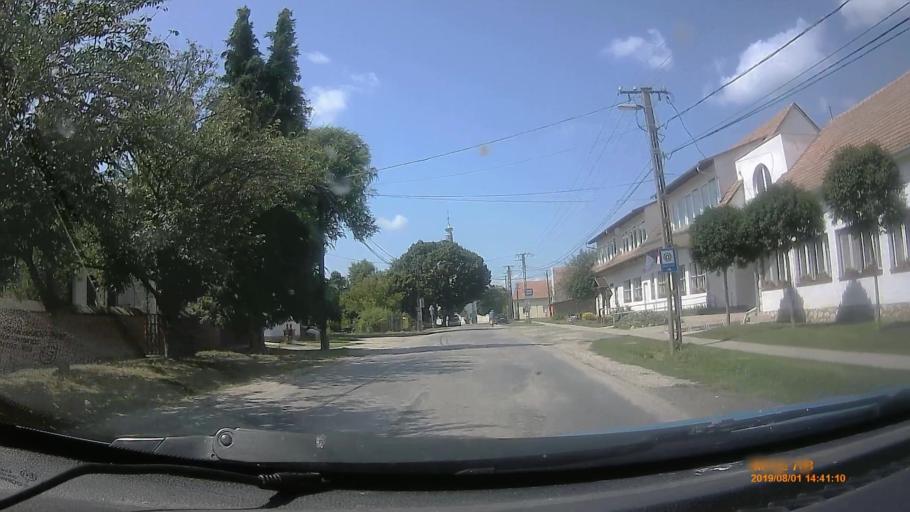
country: HR
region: Osjecko-Baranjska
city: Viljevo
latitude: 45.8236
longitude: 18.1019
